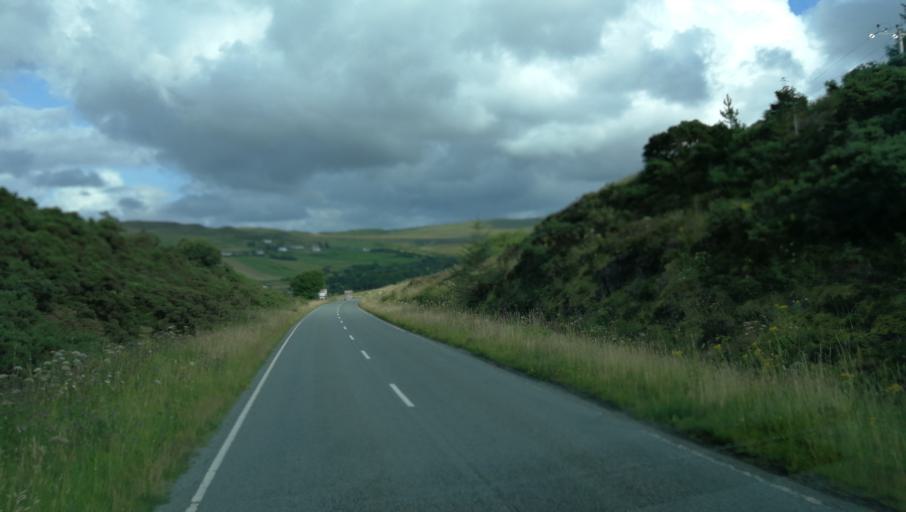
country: GB
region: Scotland
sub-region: Highland
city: Isle of Skye
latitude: 57.4722
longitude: -6.4443
